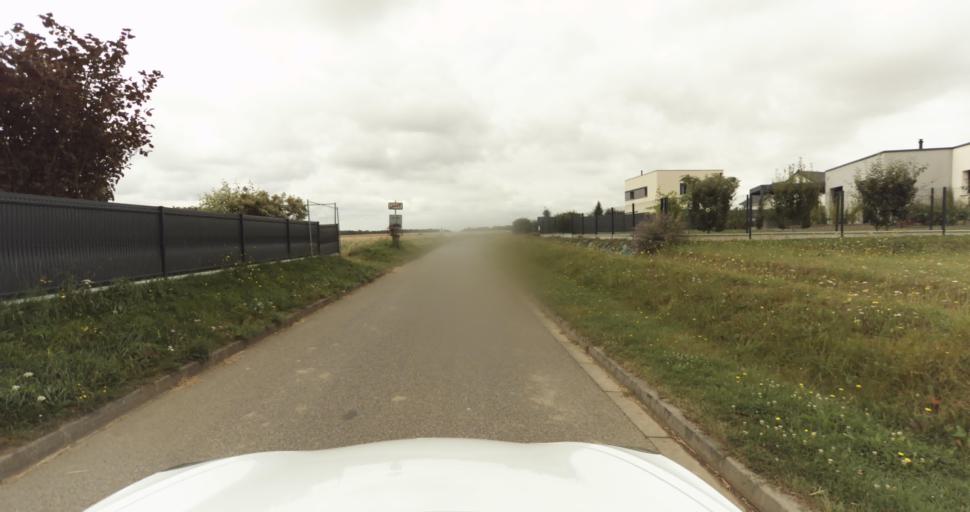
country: FR
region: Haute-Normandie
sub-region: Departement de l'Eure
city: Claville
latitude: 49.0235
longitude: 1.0306
